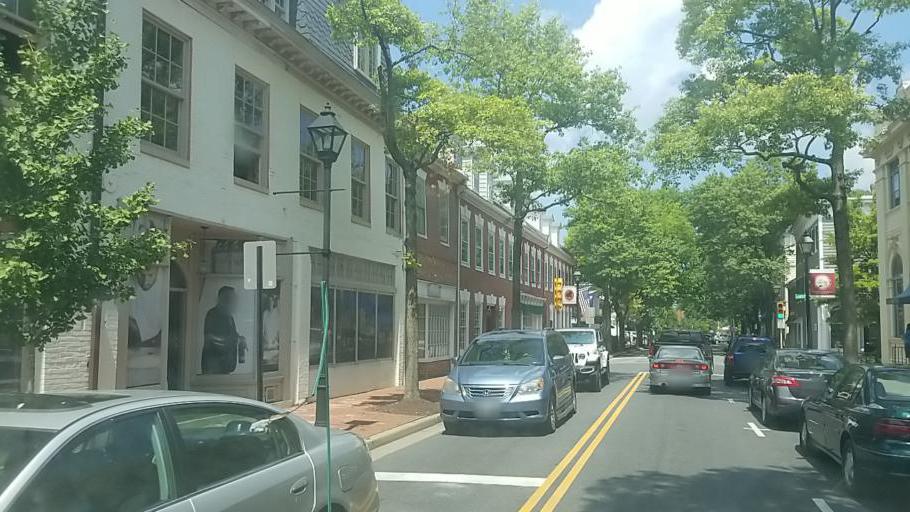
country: US
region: Maryland
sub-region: Talbot County
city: Easton
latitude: 38.7753
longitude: -76.0763
